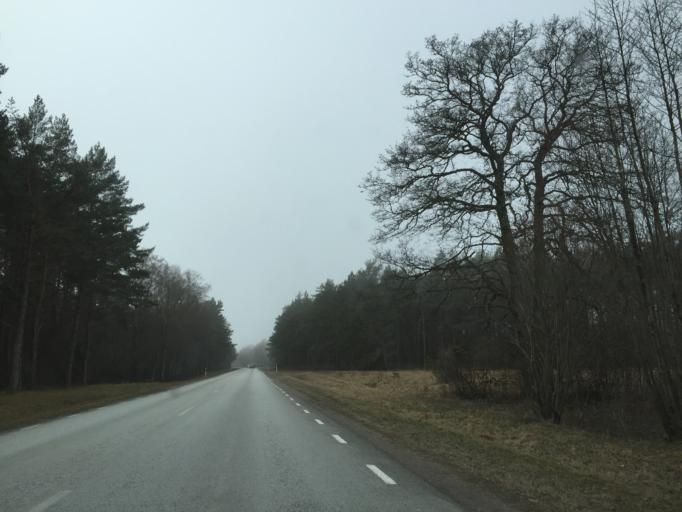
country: EE
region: Saare
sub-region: Kuressaare linn
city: Kuressaare
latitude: 58.2114
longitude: 22.3110
